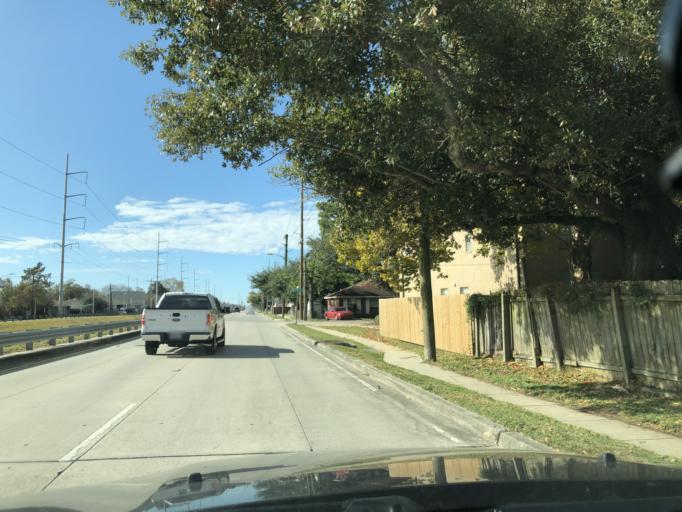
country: US
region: Louisiana
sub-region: Jefferson Parish
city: Metairie Terrace
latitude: 29.9930
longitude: -90.1666
